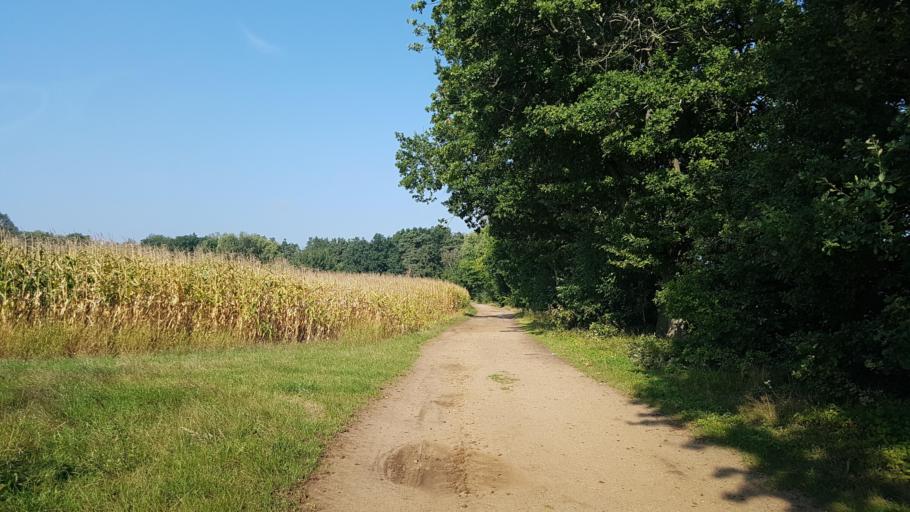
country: DE
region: Brandenburg
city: Luckau
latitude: 51.7981
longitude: 13.6547
